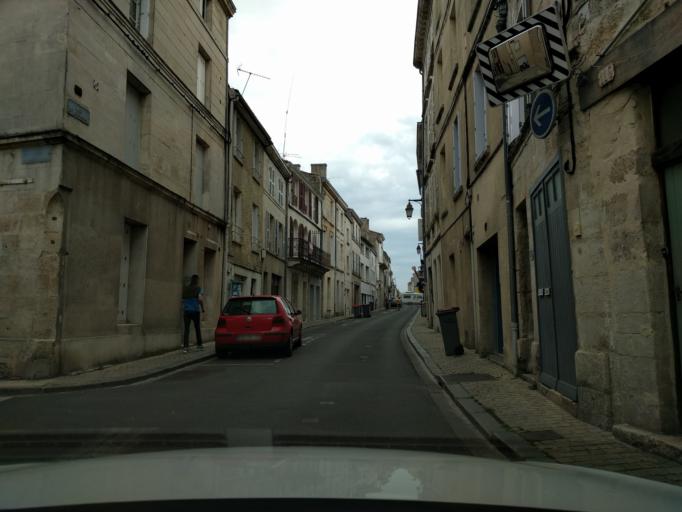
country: FR
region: Poitou-Charentes
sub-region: Departement des Deux-Sevres
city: Niort
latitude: 46.3283
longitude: -0.4592
